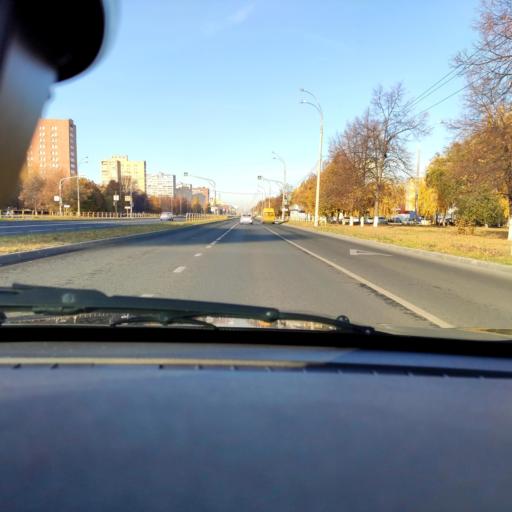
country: RU
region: Samara
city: Tol'yatti
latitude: 53.5257
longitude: 49.3195
